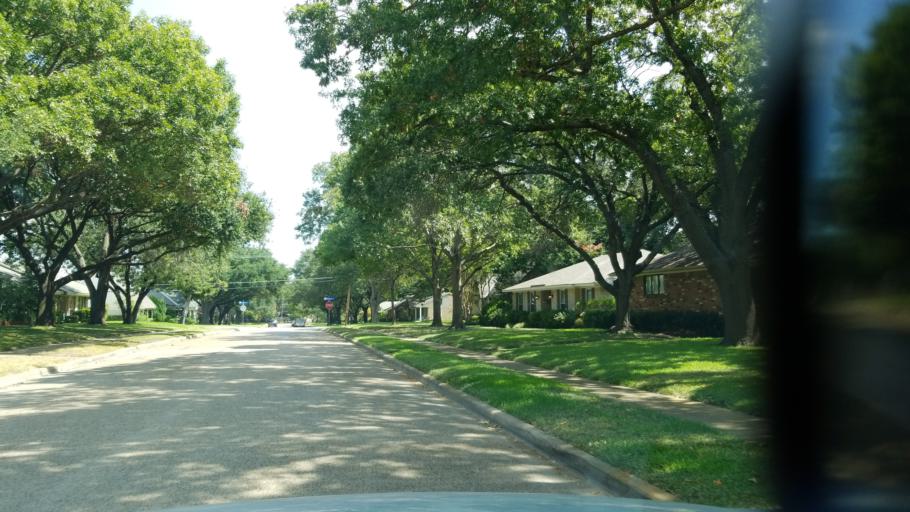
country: US
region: Texas
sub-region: Dallas County
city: Richardson
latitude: 32.9663
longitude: -96.7633
